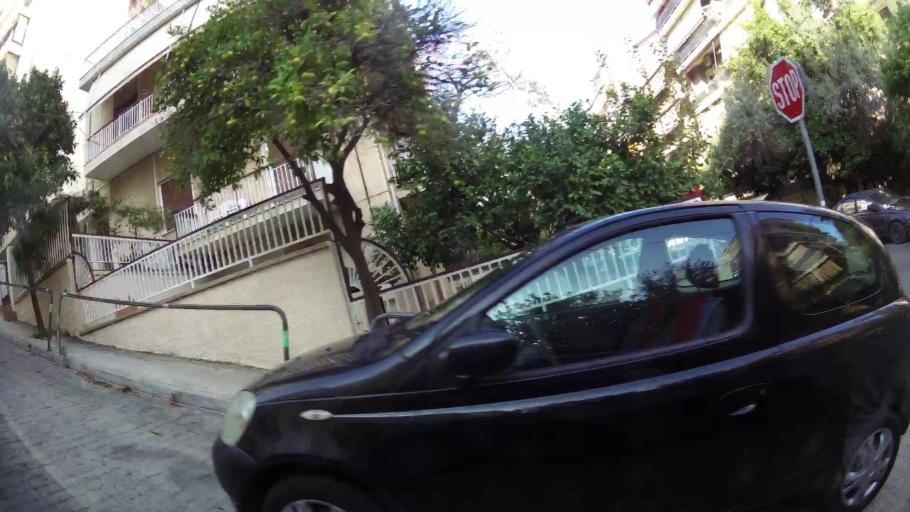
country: GR
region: Attica
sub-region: Nomarchia Athinas
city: Kaisariani
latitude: 37.9739
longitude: 23.7696
